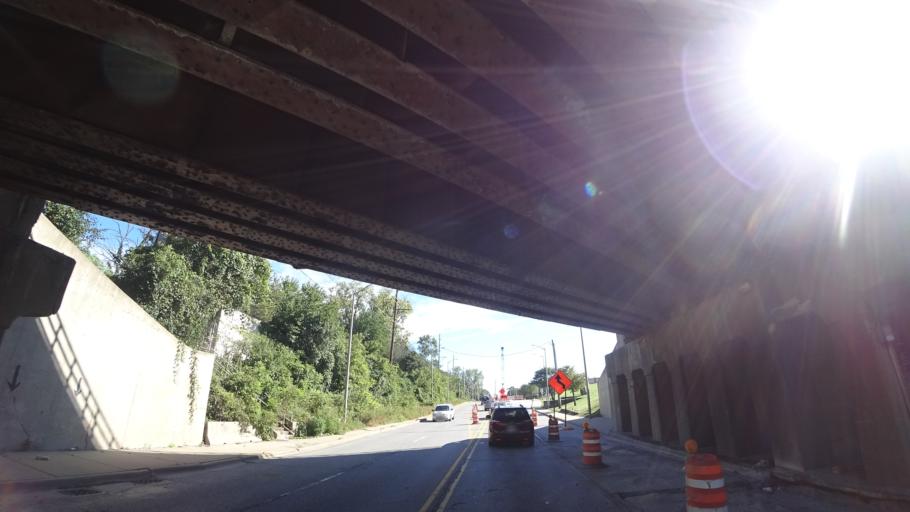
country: US
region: Illinois
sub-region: Cook County
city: Oak Forest
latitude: 41.6061
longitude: -87.7366
